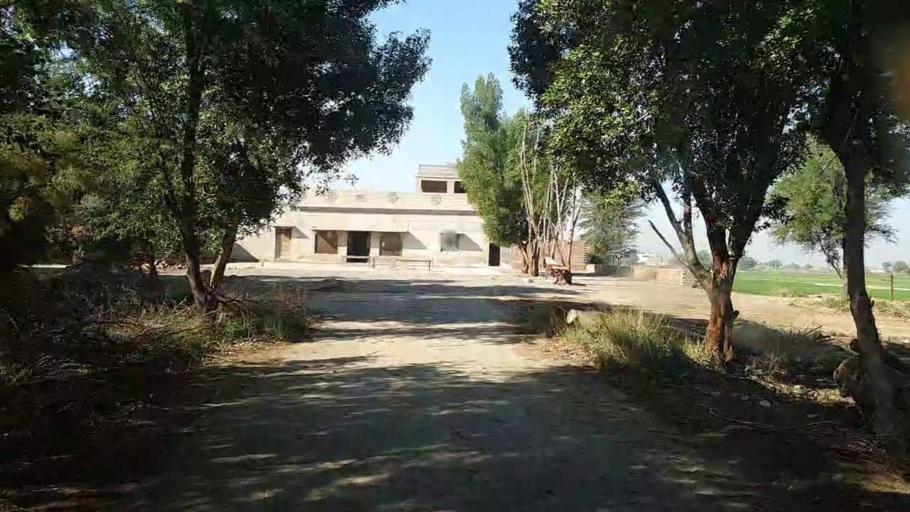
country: PK
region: Sindh
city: Khairpur
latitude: 28.0515
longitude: 69.7479
